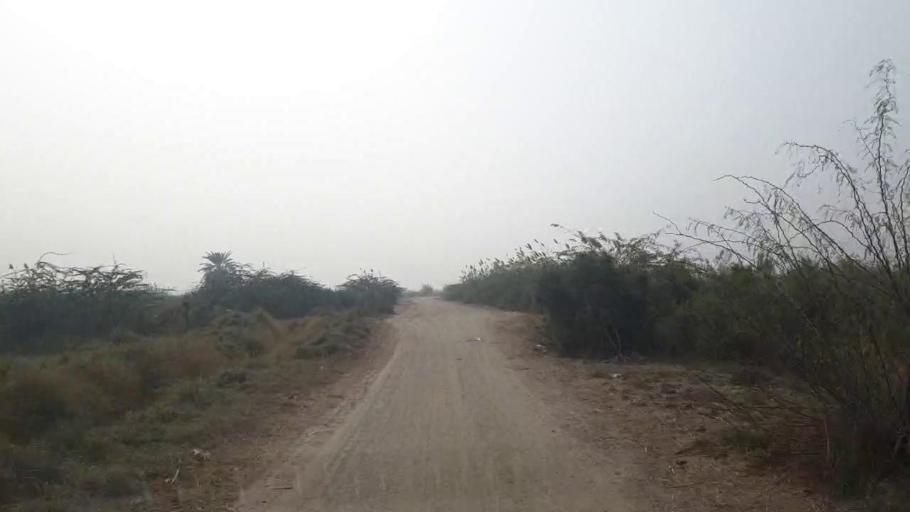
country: PK
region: Sindh
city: Bhit Shah
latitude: 25.7911
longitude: 68.5583
